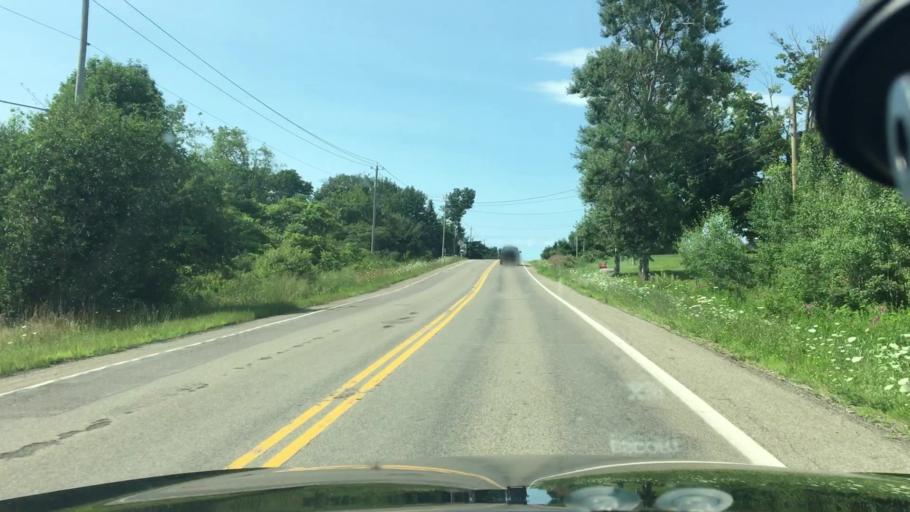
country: US
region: New York
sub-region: Chautauqua County
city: Mayville
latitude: 42.2612
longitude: -79.3482
